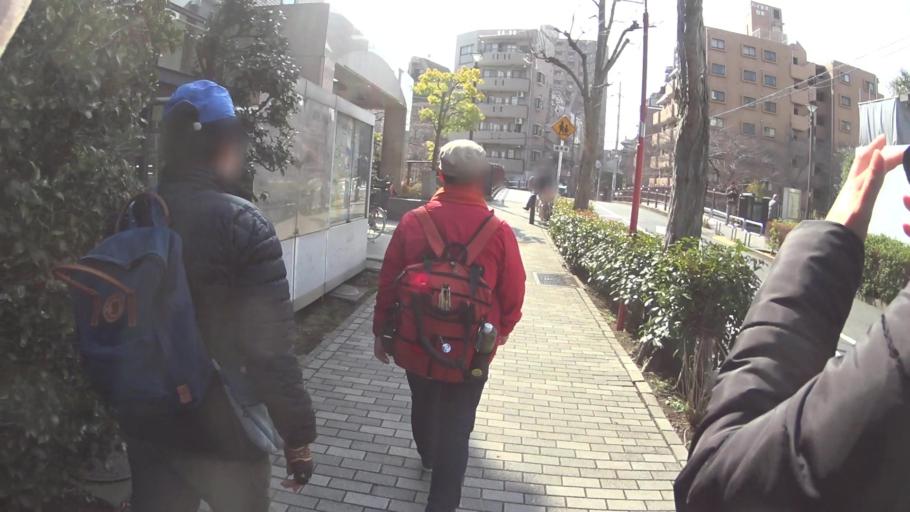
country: JP
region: Tokyo
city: Tokyo
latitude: 35.6368
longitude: 139.7079
